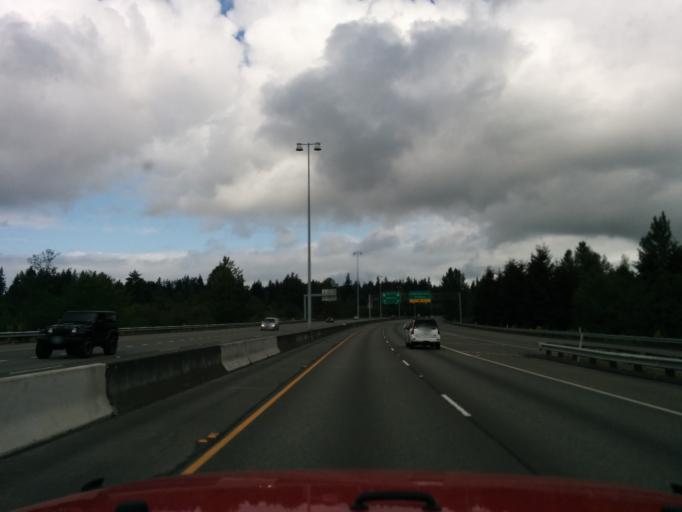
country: US
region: Washington
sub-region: Snohomish County
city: Alderwood Manor
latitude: 47.8348
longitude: -122.2674
